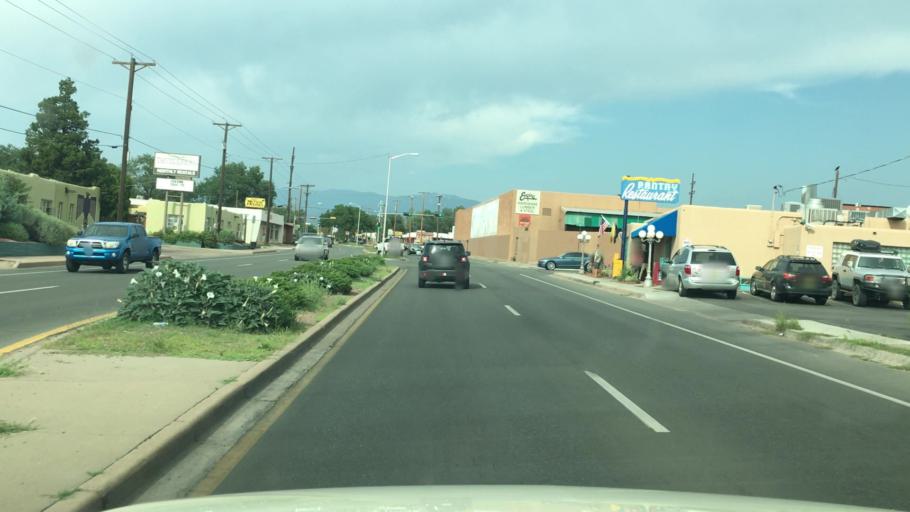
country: US
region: New Mexico
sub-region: Santa Fe County
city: Santa Fe
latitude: 35.6648
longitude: -105.9729
